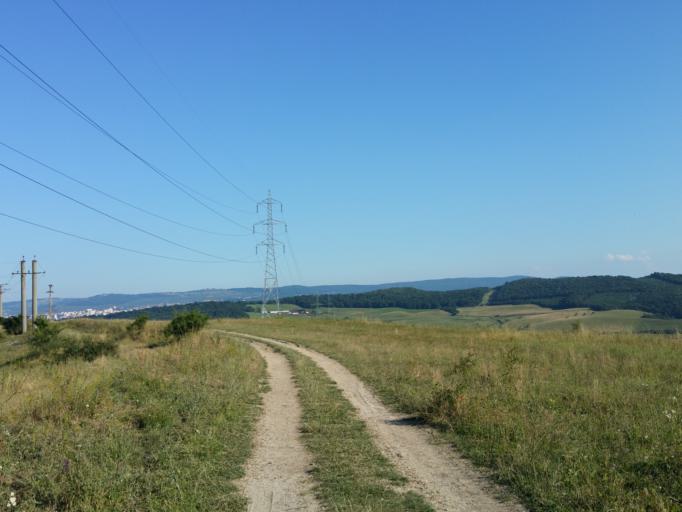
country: RO
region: Cluj
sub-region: Comuna Baciu
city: Baciu
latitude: 46.7947
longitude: 23.5314
